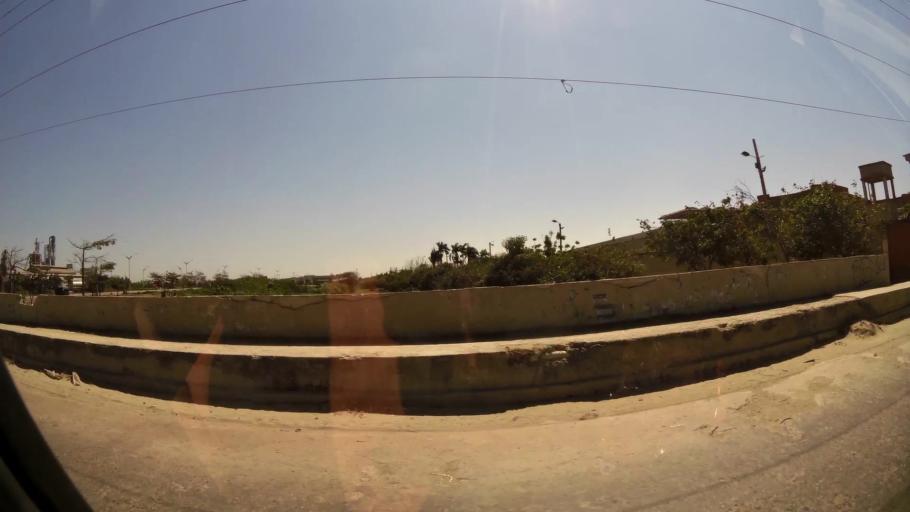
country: CO
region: Atlantico
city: Barranquilla
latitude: 10.9742
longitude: -74.7701
